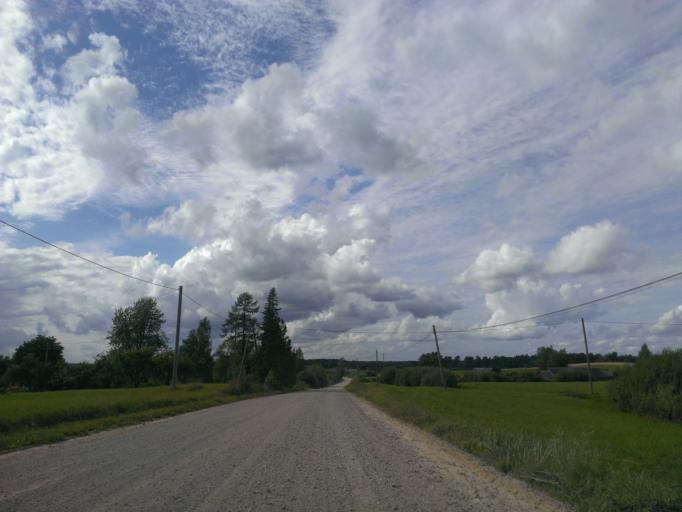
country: LV
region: Skriveri
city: Skriveri
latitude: 56.8431
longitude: 25.1780
